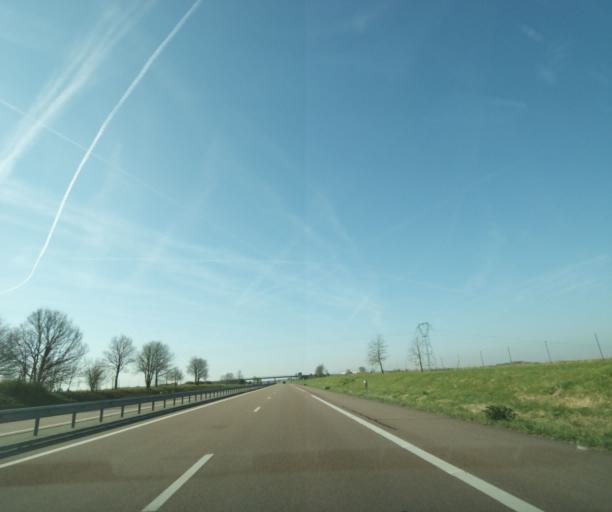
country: FR
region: Ile-de-France
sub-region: Departement de Seine-et-Marne
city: Souppes-sur-Loing
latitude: 48.2008
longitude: 2.7709
